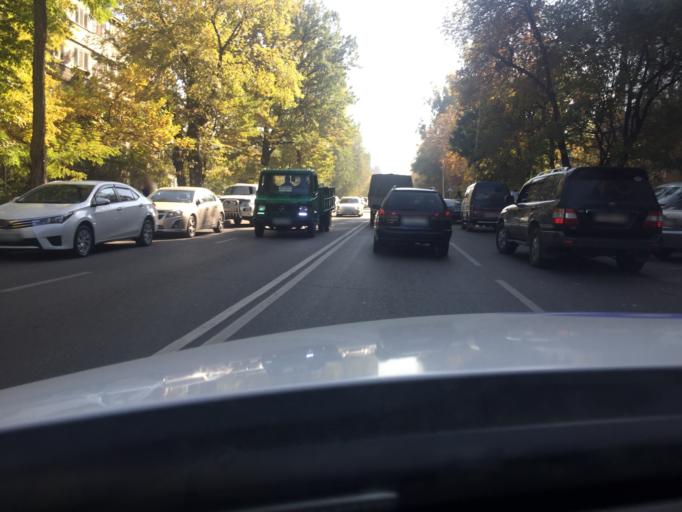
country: KZ
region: Almaty Qalasy
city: Almaty
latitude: 43.2566
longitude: 76.9110
